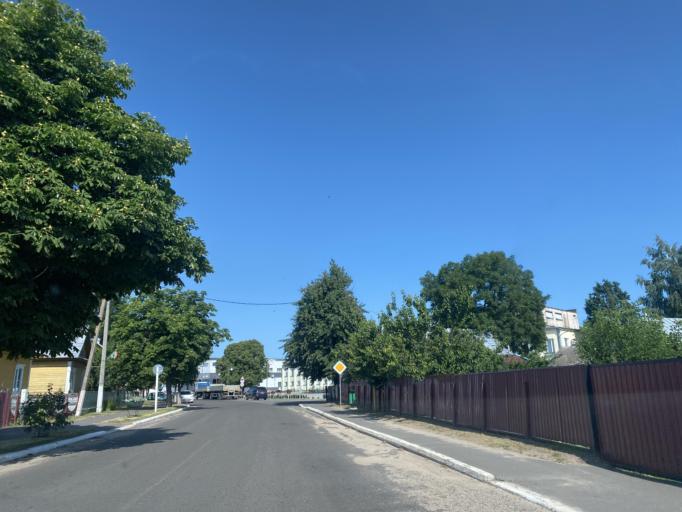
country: BY
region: Brest
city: Ivanava
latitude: 52.3161
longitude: 25.6110
